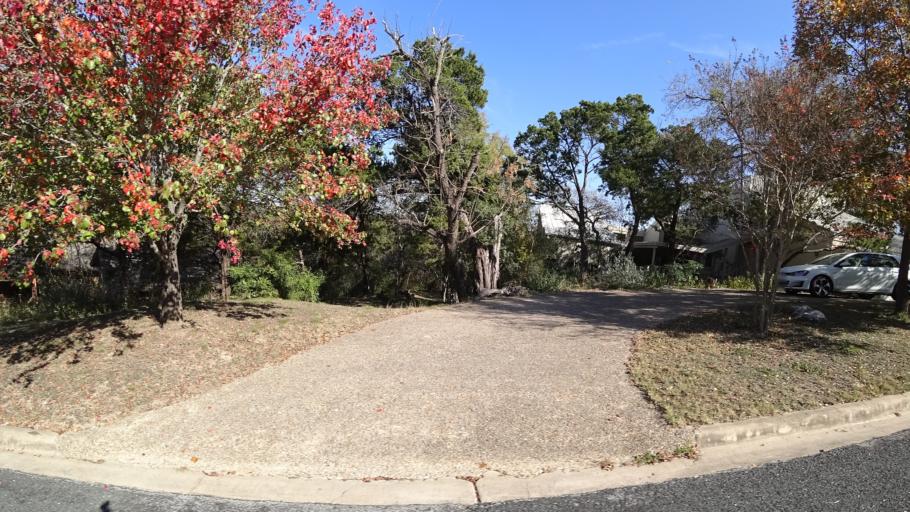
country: US
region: Texas
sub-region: Williamson County
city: Jollyville
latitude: 30.3713
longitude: -97.7703
